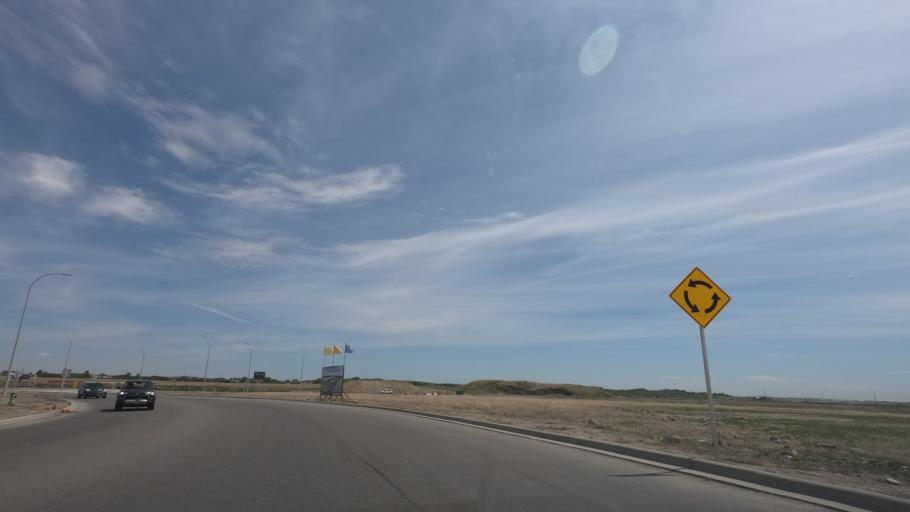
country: CA
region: Alberta
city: Airdrie
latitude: 51.2525
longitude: -114.0072
